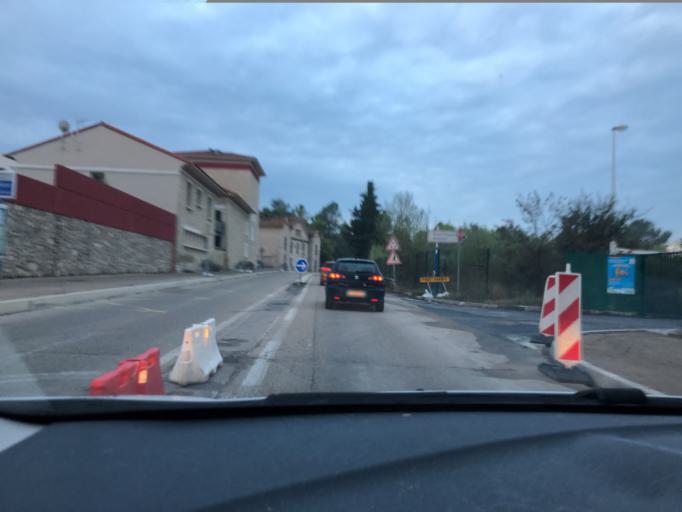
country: FR
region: Languedoc-Roussillon
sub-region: Departement de l'Herault
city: Montferrier-sur-Lez
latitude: 43.6752
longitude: 3.8673
